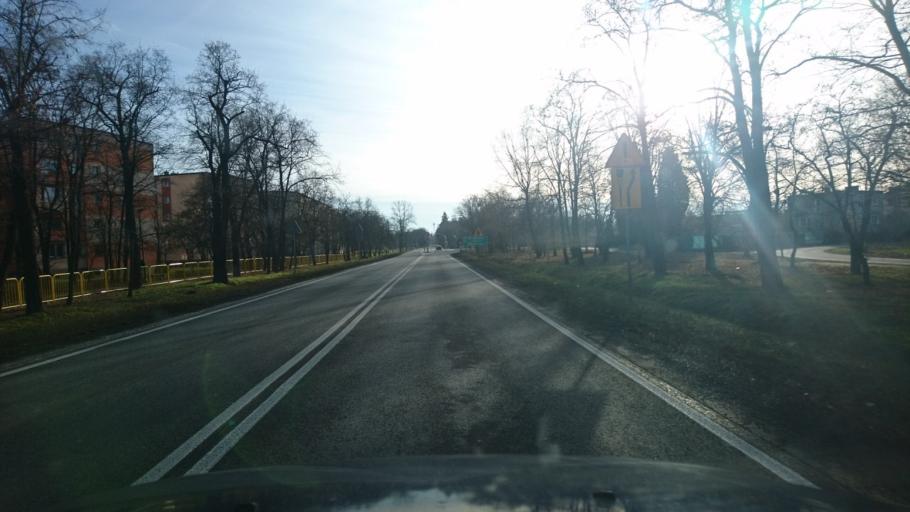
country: PL
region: Greater Poland Voivodeship
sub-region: Powiat ostrzeszowski
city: Ostrzeszow
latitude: 51.4307
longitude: 17.9190
